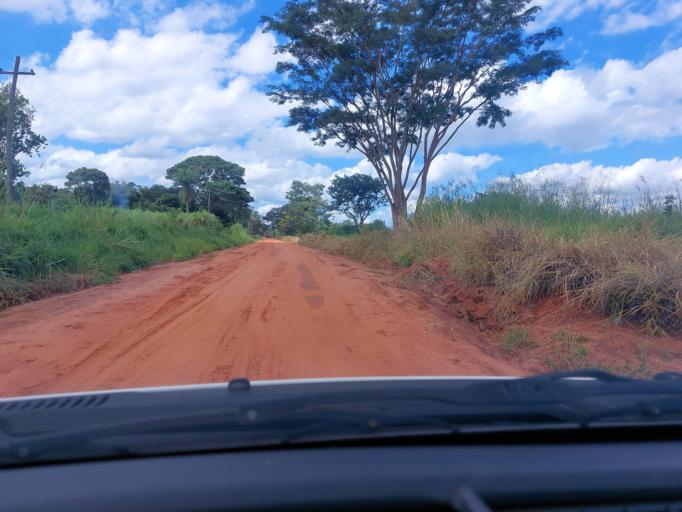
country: PY
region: San Pedro
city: Itacurubi del Rosario
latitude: -24.5364
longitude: -56.5709
